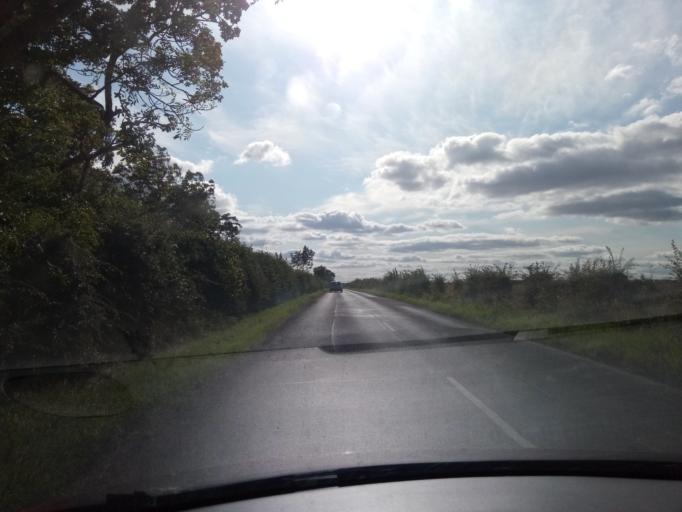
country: GB
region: Scotland
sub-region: The Scottish Borders
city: Allanton
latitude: 55.7403
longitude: -2.1885
